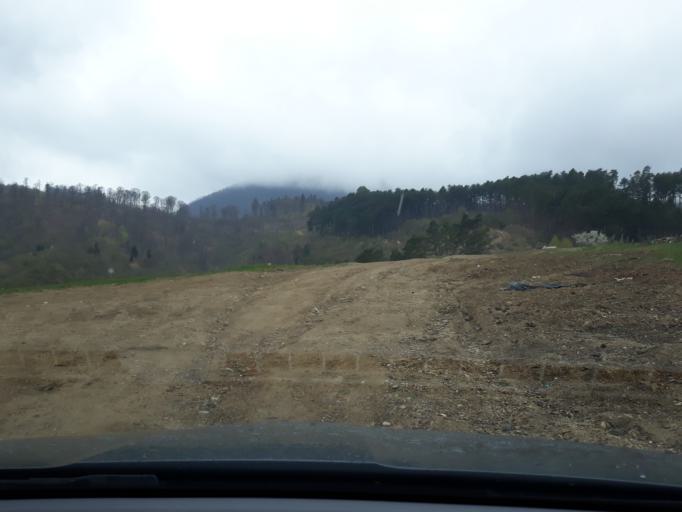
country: RO
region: Brasov
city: Codlea
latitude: 45.6944
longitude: 25.4335
